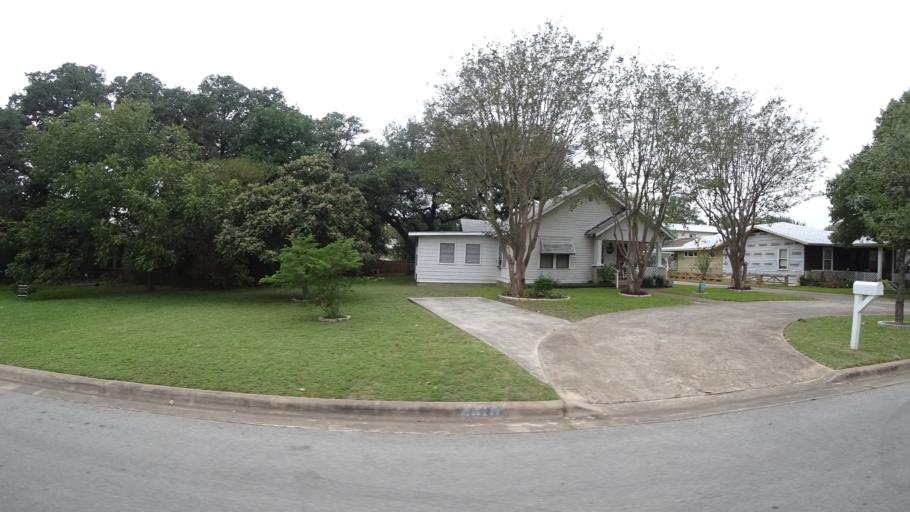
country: US
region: Texas
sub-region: Travis County
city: Austin
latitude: 30.2185
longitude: -97.7703
